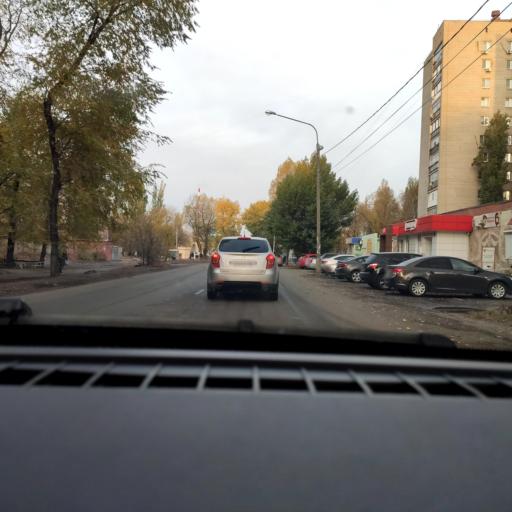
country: RU
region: Voronezj
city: Voronezh
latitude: 51.6378
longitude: 39.2675
